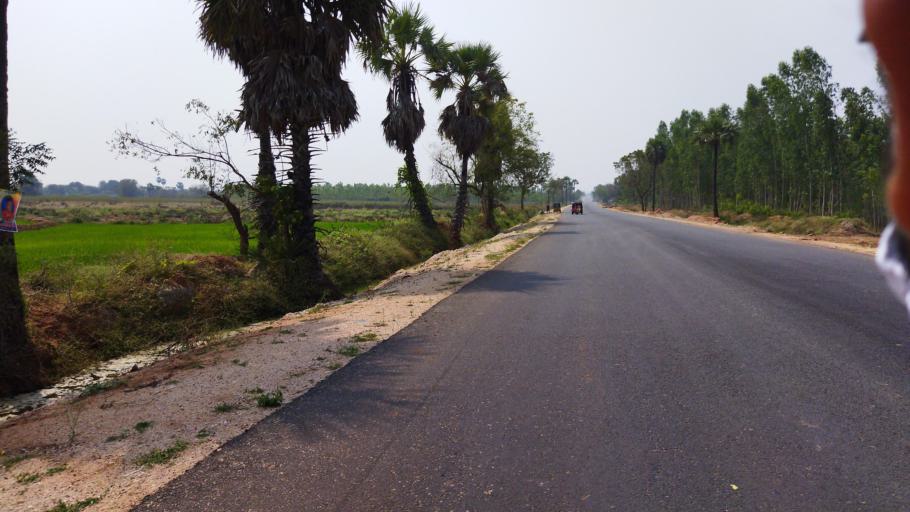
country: IN
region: Telangana
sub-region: Nalgonda
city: Nalgonda
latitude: 17.1537
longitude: 79.4088
